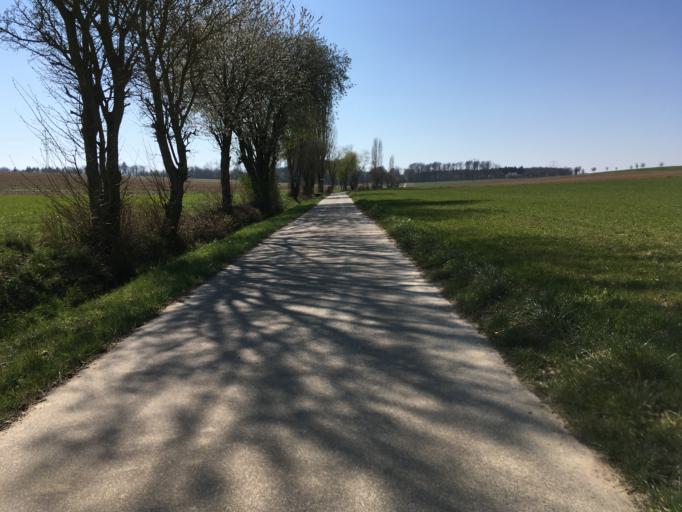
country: DE
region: Baden-Wuerttemberg
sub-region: Regierungsbezirk Stuttgart
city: Massenbachhausen
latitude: 49.1956
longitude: 9.0851
